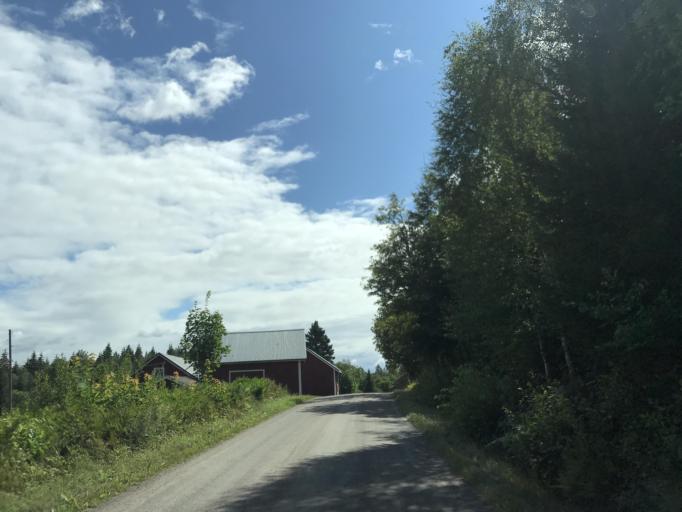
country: FI
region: Uusimaa
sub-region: Helsinki
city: Kaerkoelae
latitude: 60.6313
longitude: 23.8387
